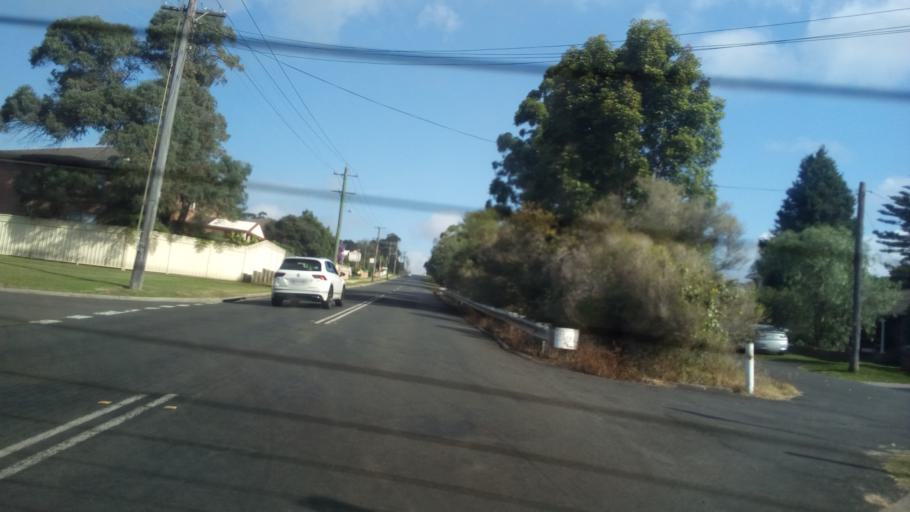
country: AU
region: New South Wales
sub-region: Wollongong
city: Helensburgh
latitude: -34.1959
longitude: 150.9811
